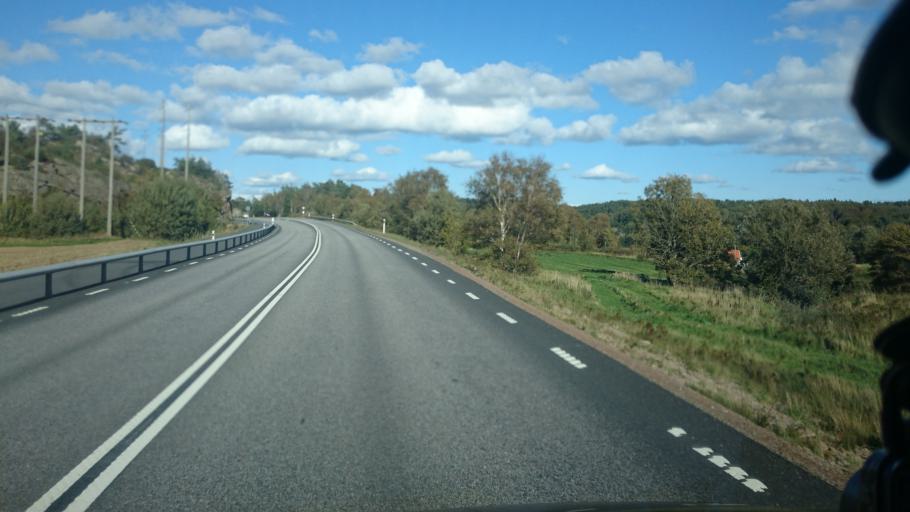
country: SE
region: Vaestra Goetaland
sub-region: Lysekils Kommun
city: Lysekil
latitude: 58.3066
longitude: 11.4793
